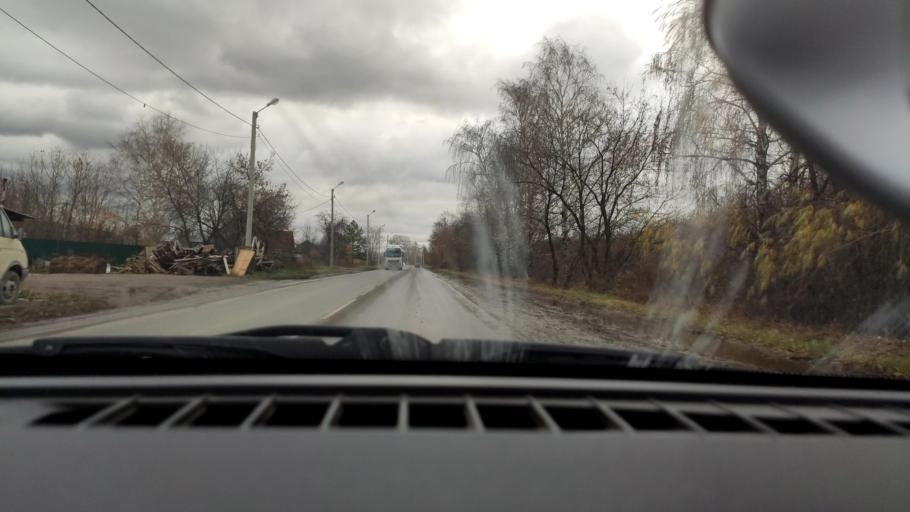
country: RU
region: Perm
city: Kondratovo
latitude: 57.9491
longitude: 56.1404
